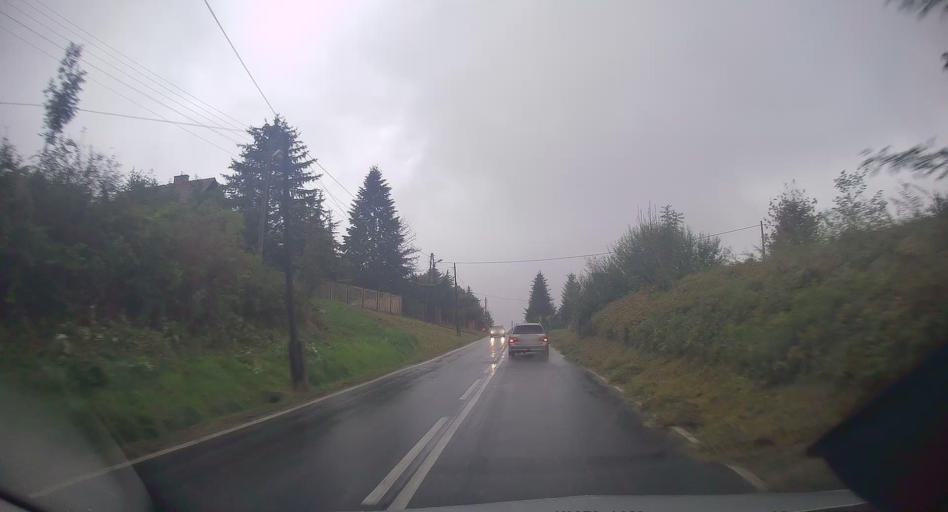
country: PL
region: Lesser Poland Voivodeship
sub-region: Powiat krakowski
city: Ochojno
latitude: 49.9832
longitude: 19.9936
